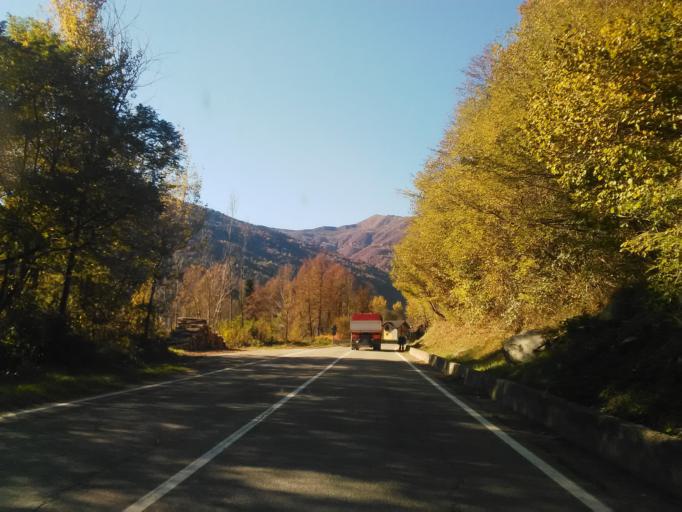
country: IT
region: Piedmont
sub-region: Provincia di Vercelli
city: Scopello
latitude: 45.7783
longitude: 8.1005
